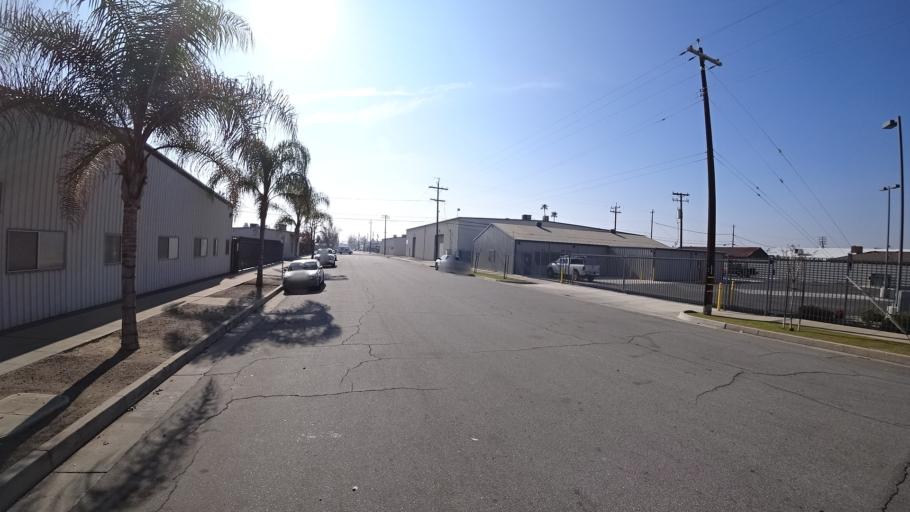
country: US
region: California
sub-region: Kern County
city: Bakersfield
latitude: 35.3783
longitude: -118.9991
